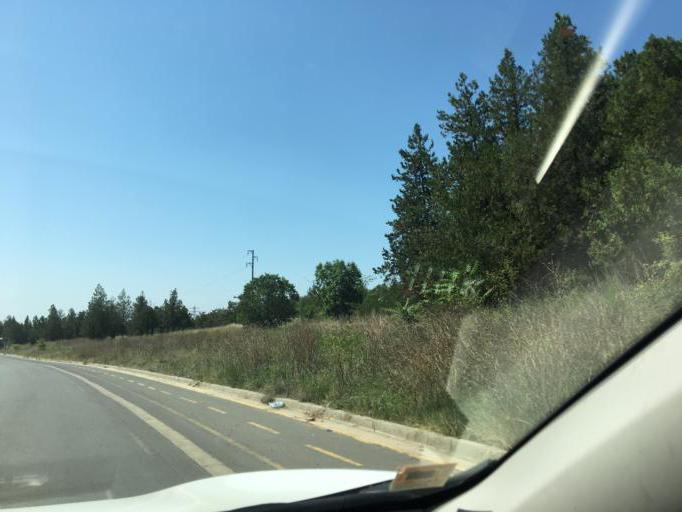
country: BG
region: Burgas
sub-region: Obshtina Kameno
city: Kameno
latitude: 42.6185
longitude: 27.3943
